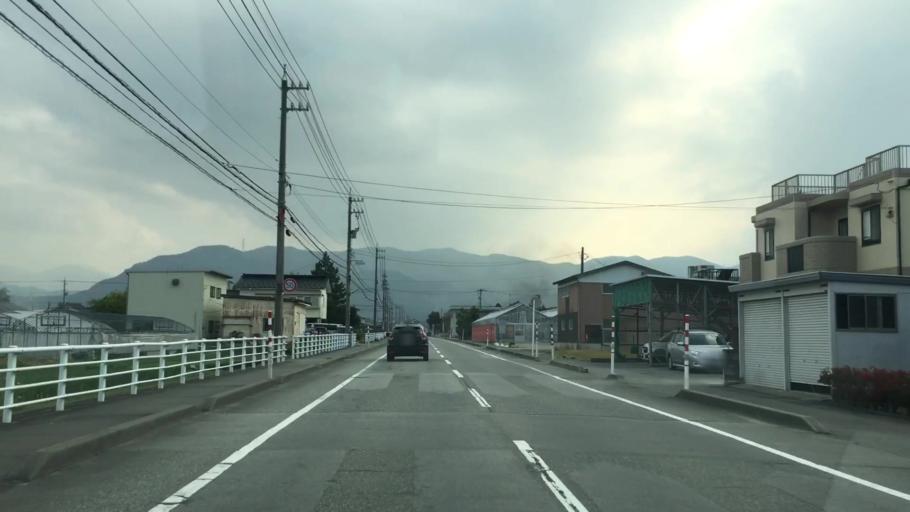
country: JP
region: Toyama
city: Yatsuomachi-higashikumisaka
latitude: 36.5869
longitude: 137.1911
